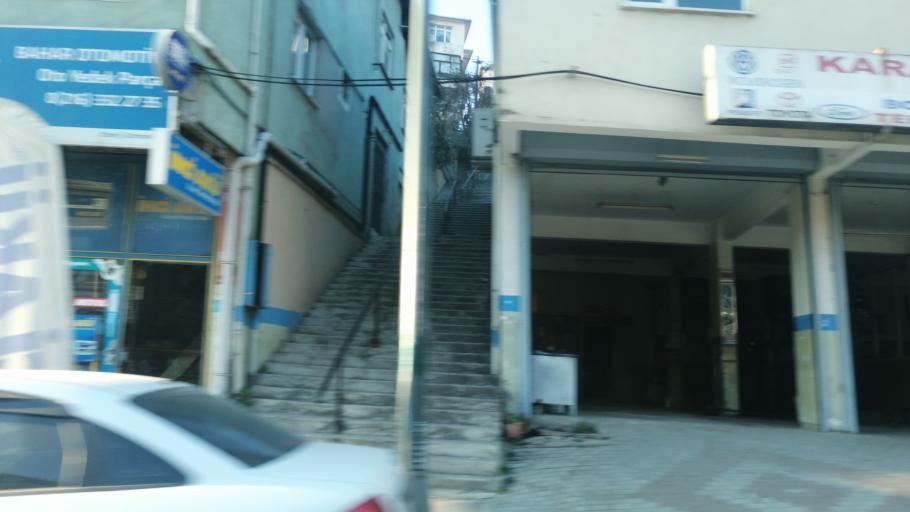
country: TR
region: Istanbul
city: UEskuedar
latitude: 41.0522
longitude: 29.0663
